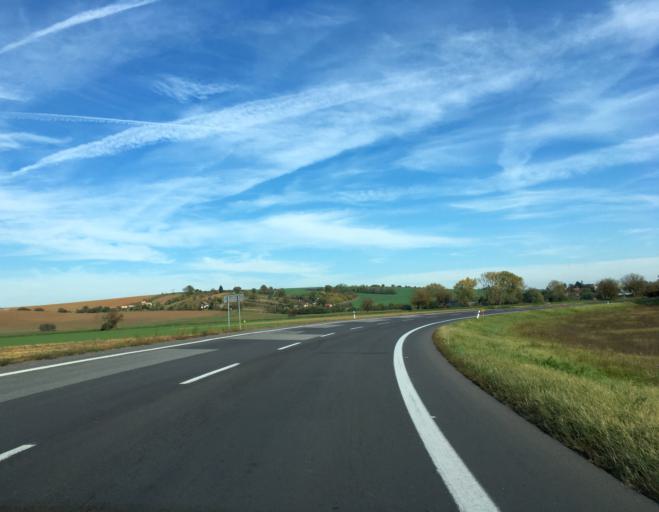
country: SK
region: Banskobystricky
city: Dudince
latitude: 48.1653
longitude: 18.8693
